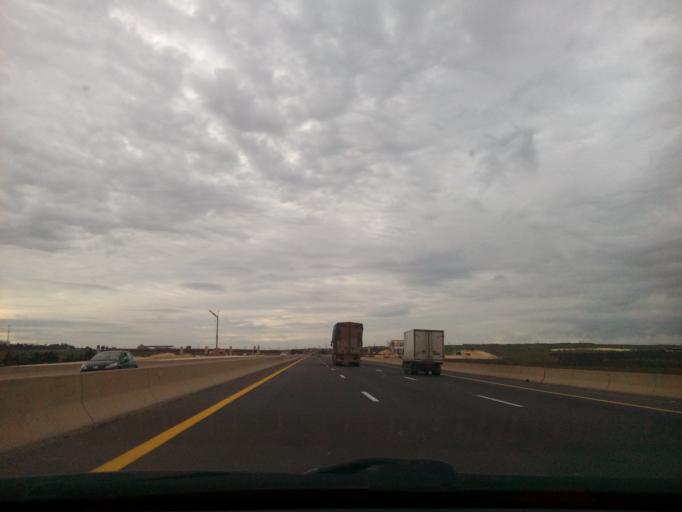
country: DZ
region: Mascara
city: Sig
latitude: 35.5420
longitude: -0.3506
